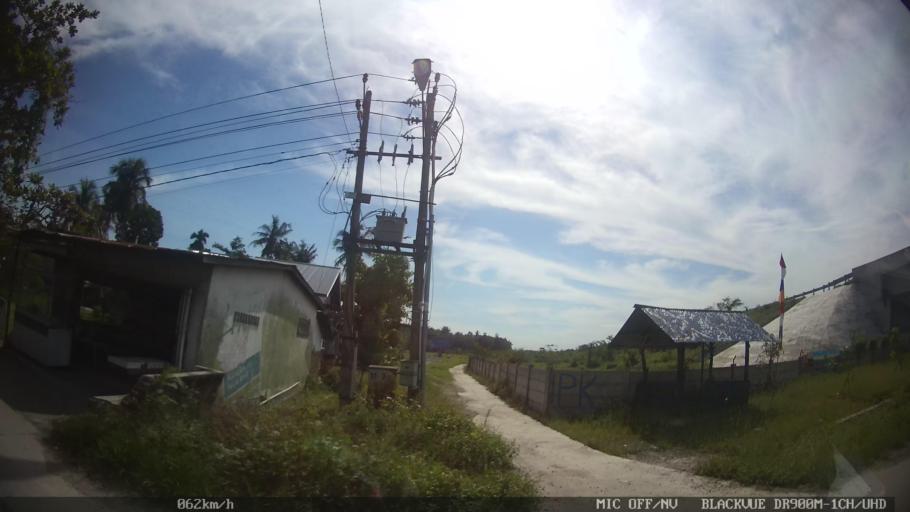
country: ID
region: North Sumatra
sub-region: Kabupaten Langkat
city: Stabat
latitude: 3.7143
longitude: 98.5046
